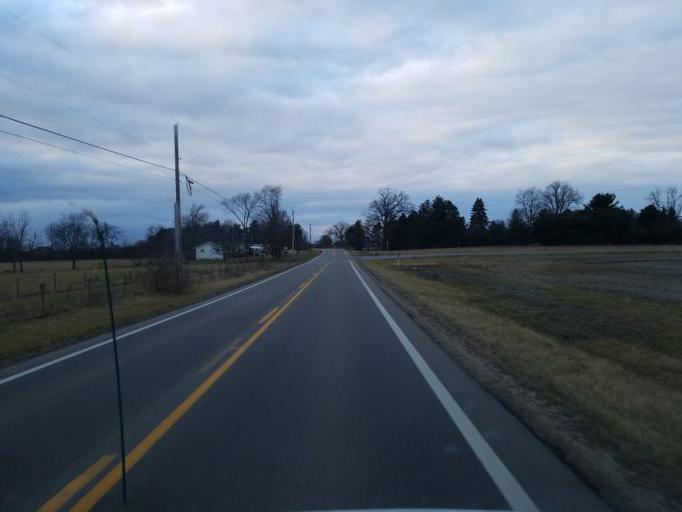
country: US
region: Ohio
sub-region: Delaware County
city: Delaware
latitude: 40.3364
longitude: -83.1329
